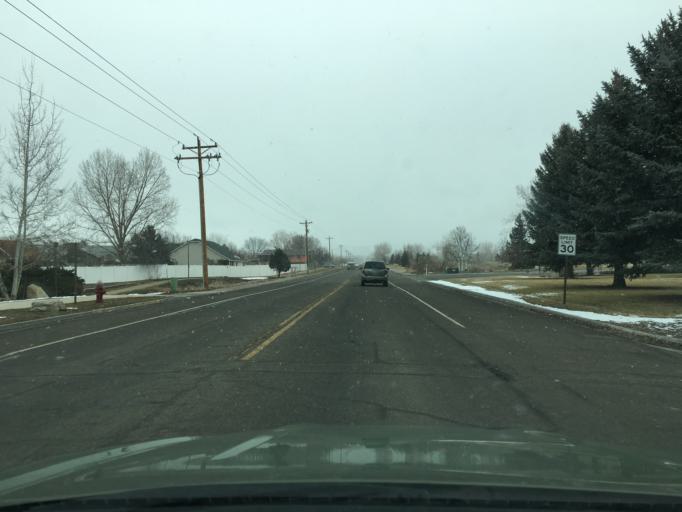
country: US
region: Colorado
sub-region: Montrose County
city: Montrose
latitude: 38.4672
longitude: -107.8610
